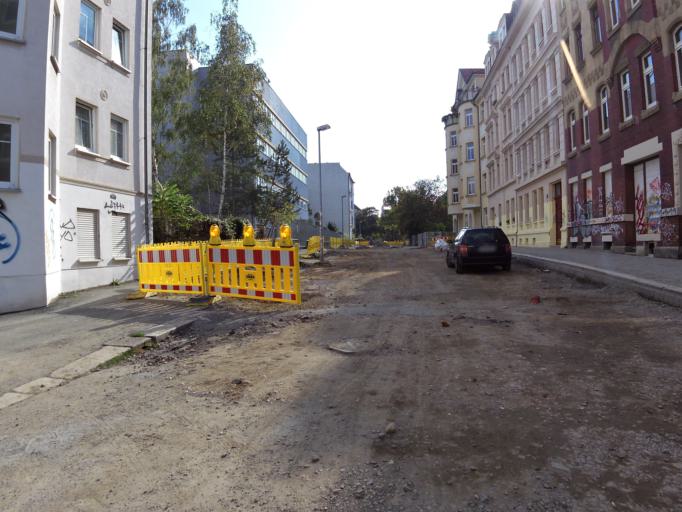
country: DE
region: Saxony
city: Leipzig
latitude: 51.3344
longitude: 12.3355
